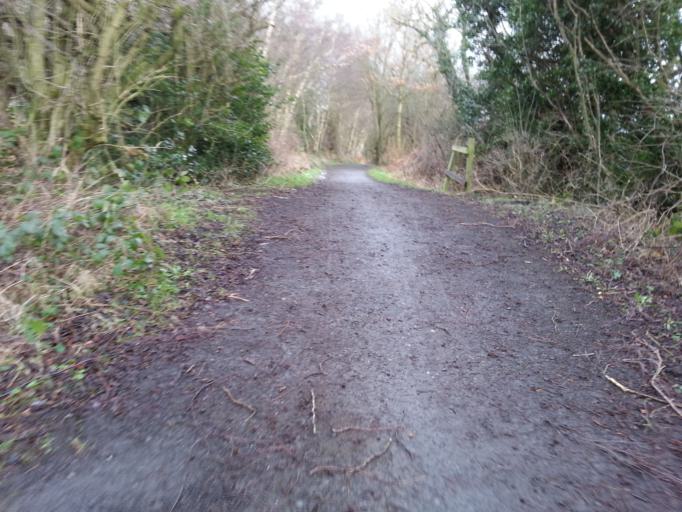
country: GB
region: England
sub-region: County Durham
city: Crook
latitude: 54.7524
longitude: -1.7325
